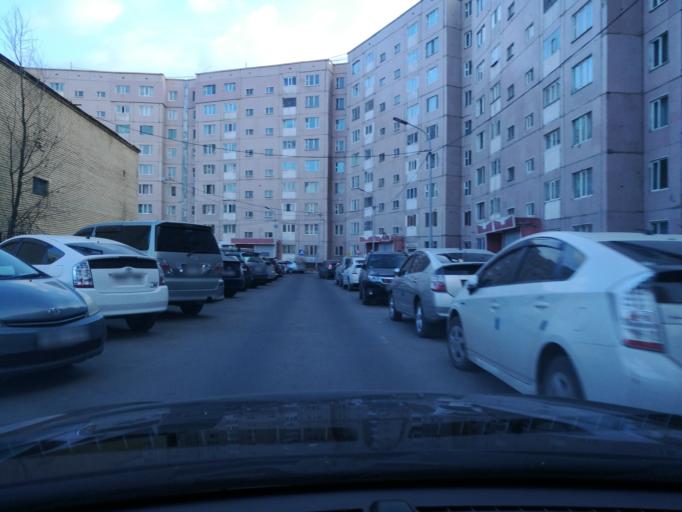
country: MN
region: Ulaanbaatar
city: Ulaanbaatar
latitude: 47.9270
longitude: 106.9280
